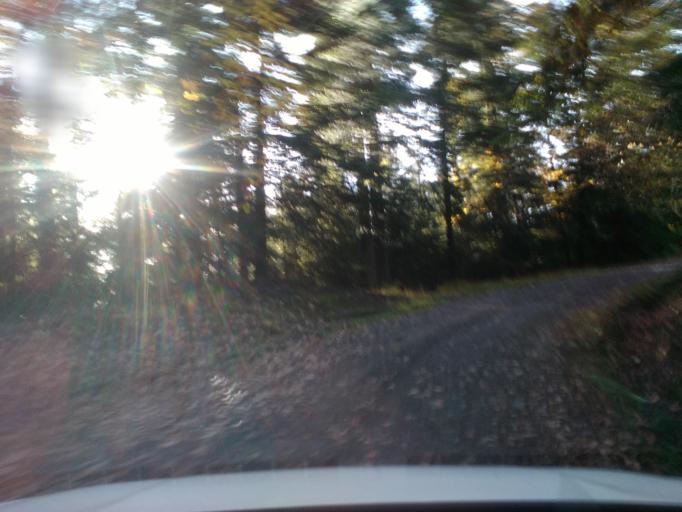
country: FR
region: Lorraine
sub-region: Departement des Vosges
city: Senones
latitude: 48.4203
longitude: 6.9933
